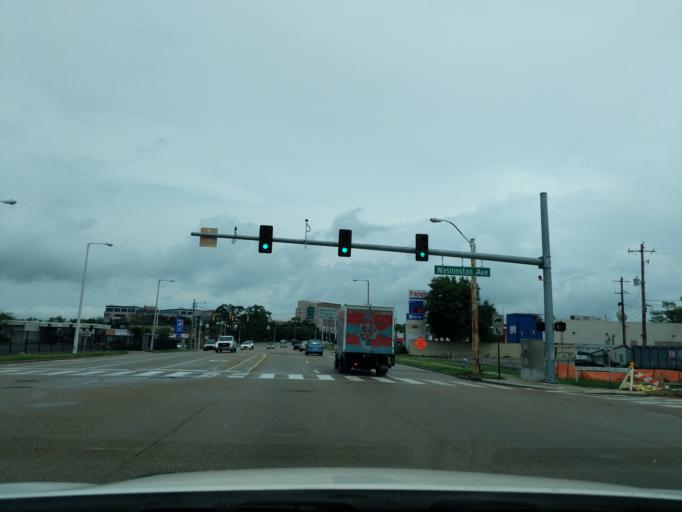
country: US
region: Tennessee
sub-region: Shelby County
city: Memphis
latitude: 35.1471
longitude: -90.0440
